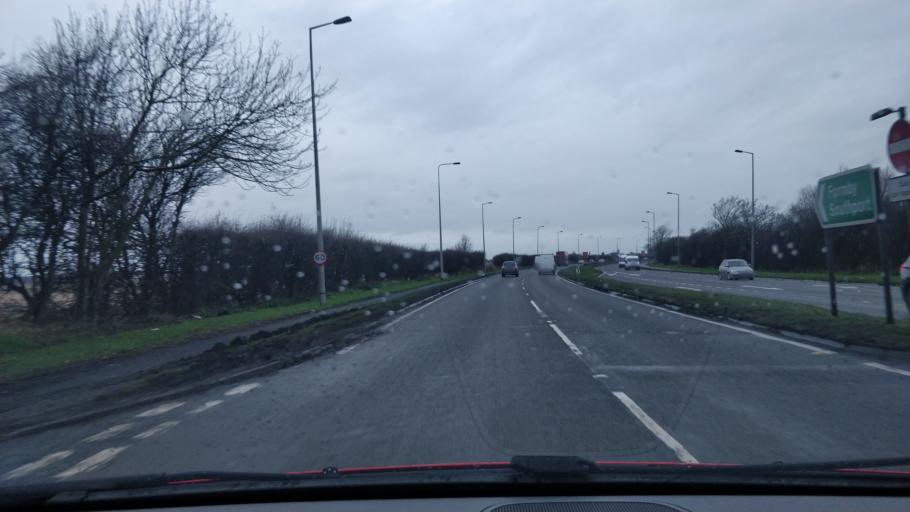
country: GB
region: England
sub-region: Sefton
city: Hightown
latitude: 53.5365
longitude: -3.0453
